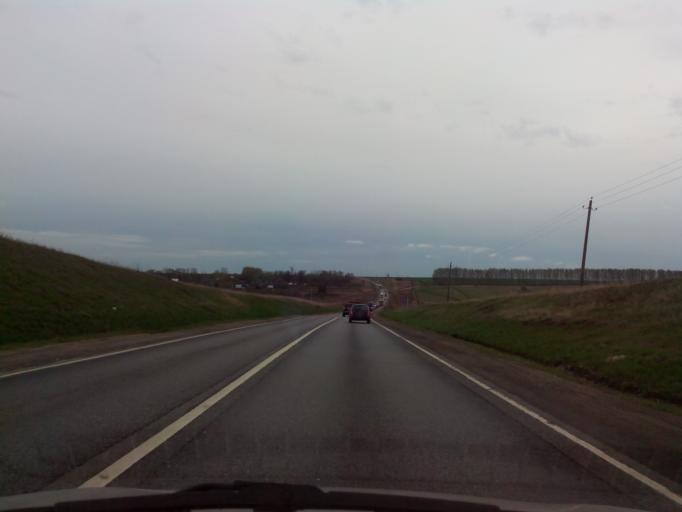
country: RU
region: Moskovskaya
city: Ozherel'ye
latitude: 54.6889
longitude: 38.3184
